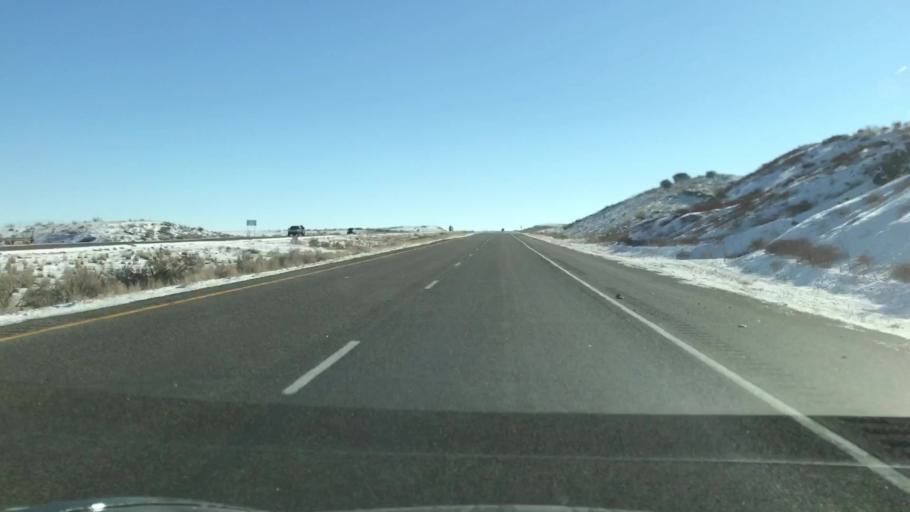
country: US
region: Colorado
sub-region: Mesa County
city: Loma
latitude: 39.2218
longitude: -108.8879
